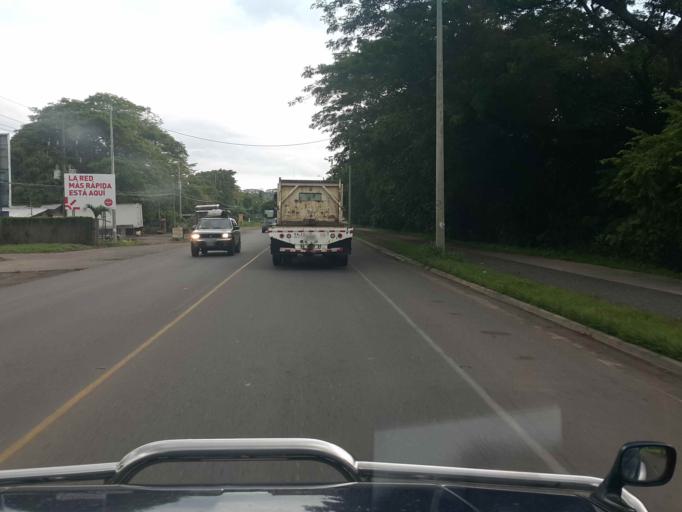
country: CR
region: Puntarenas
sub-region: Canton Central de Puntarenas
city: Chacarita
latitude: 9.9718
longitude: -84.7387
